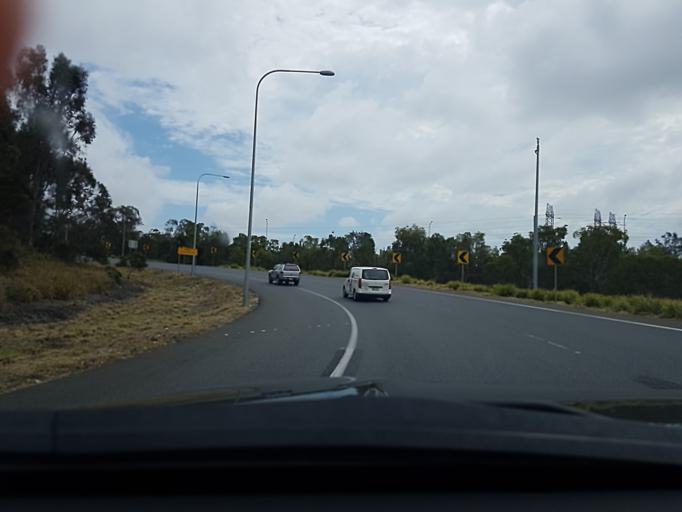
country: AU
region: Queensland
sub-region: Brisbane
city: Cannon Hill
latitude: -27.4517
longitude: 153.1134
